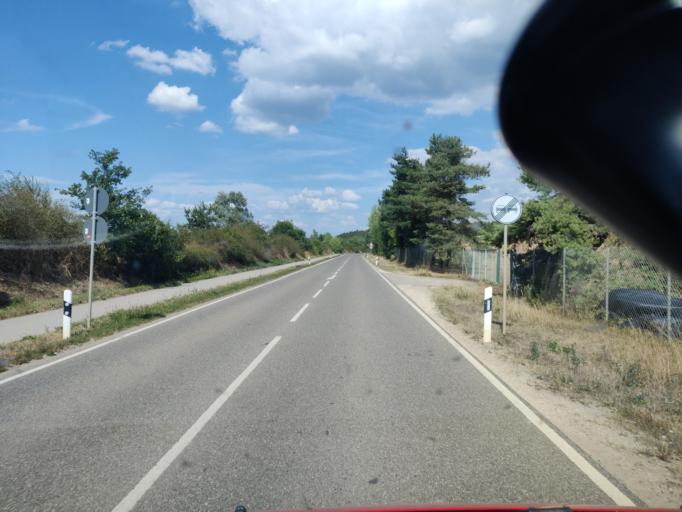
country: DE
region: Bavaria
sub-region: Regierungsbezirk Mittelfranken
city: Hilpoltstein
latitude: 49.1615
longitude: 11.1962
